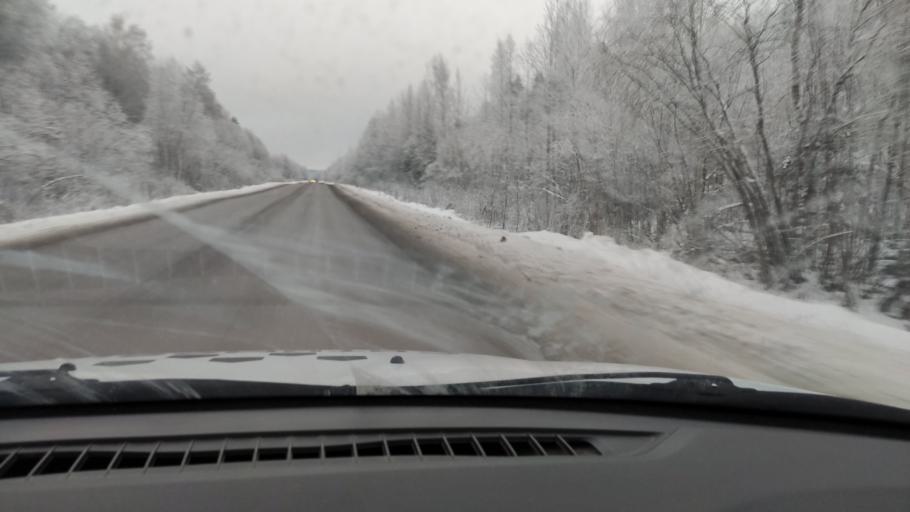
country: RU
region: Perm
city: Novyye Lyady
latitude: 58.0296
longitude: 56.6215
